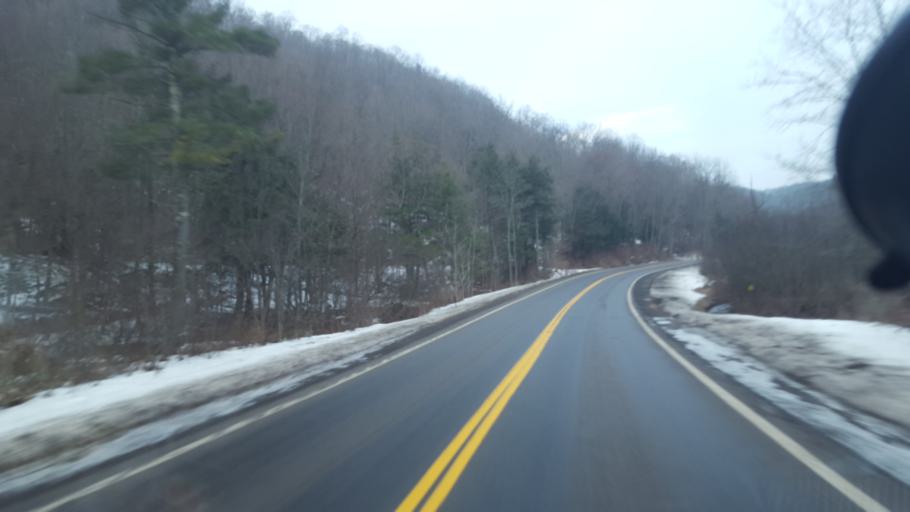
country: US
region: New York
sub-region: Allegany County
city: Andover
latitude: 42.0885
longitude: -77.6926
